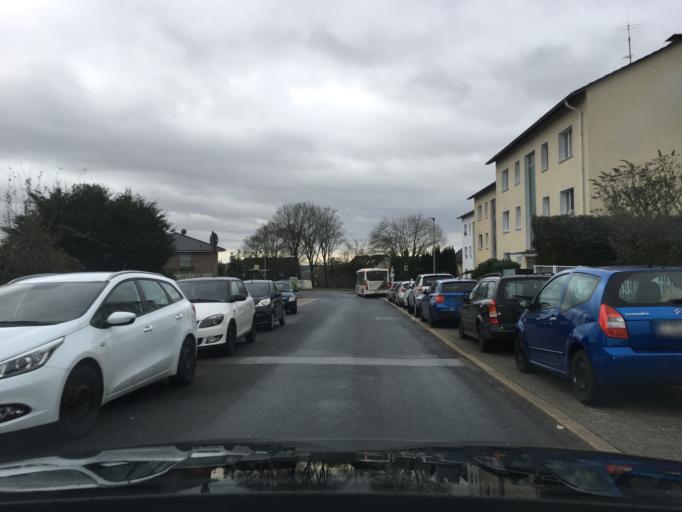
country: DE
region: North Rhine-Westphalia
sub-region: Regierungsbezirk Dusseldorf
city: Velbert
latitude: 51.3232
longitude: 7.0143
